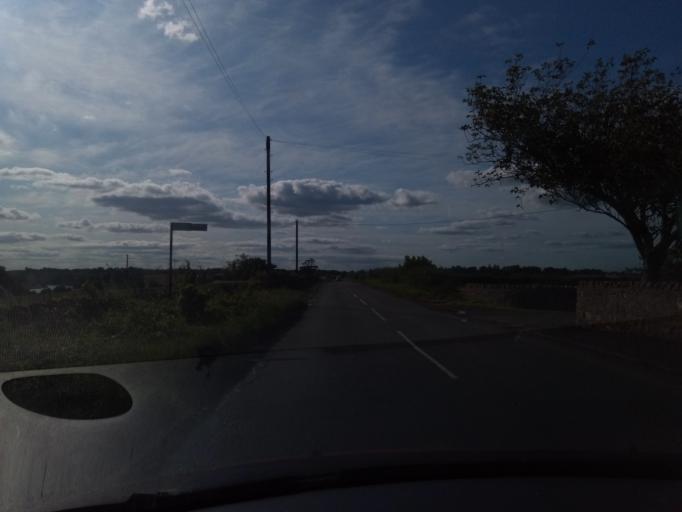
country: GB
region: England
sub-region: Northumberland
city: Berwick-Upon-Tweed
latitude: 55.7653
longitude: -2.0777
